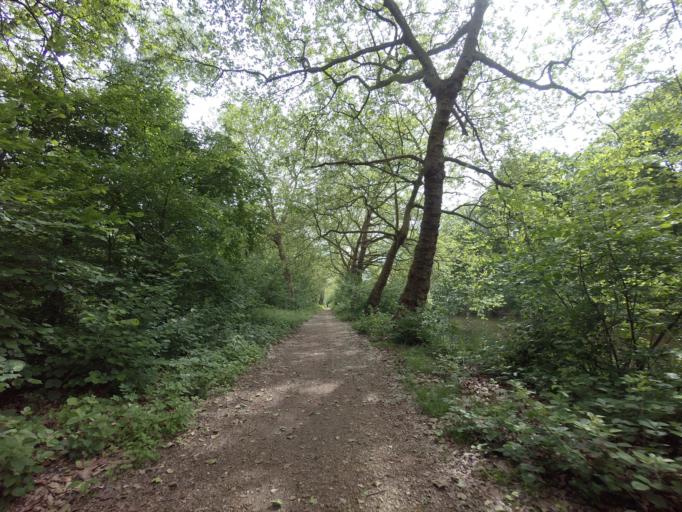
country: BE
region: Flanders
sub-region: Provincie Antwerpen
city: Bornem
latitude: 51.1081
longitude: 4.2748
